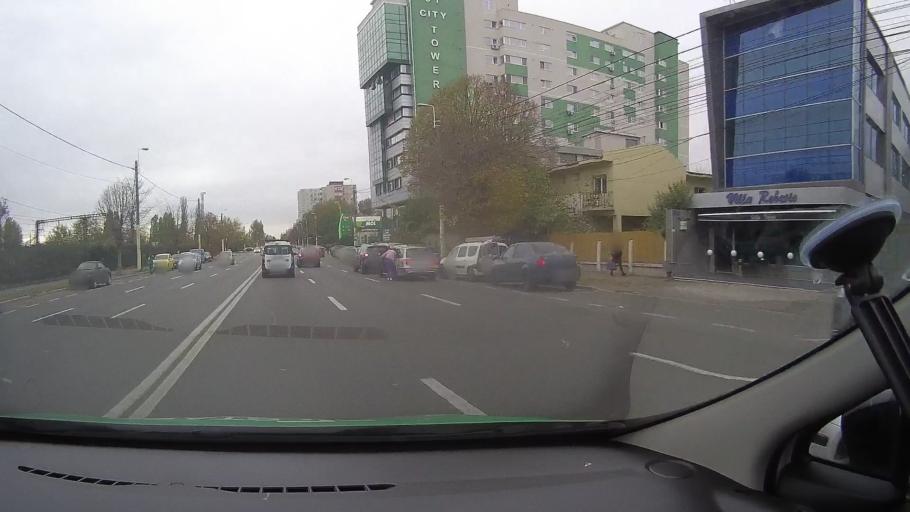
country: RO
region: Constanta
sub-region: Municipiul Constanta
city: Constanta
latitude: 44.1719
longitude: 28.6265
